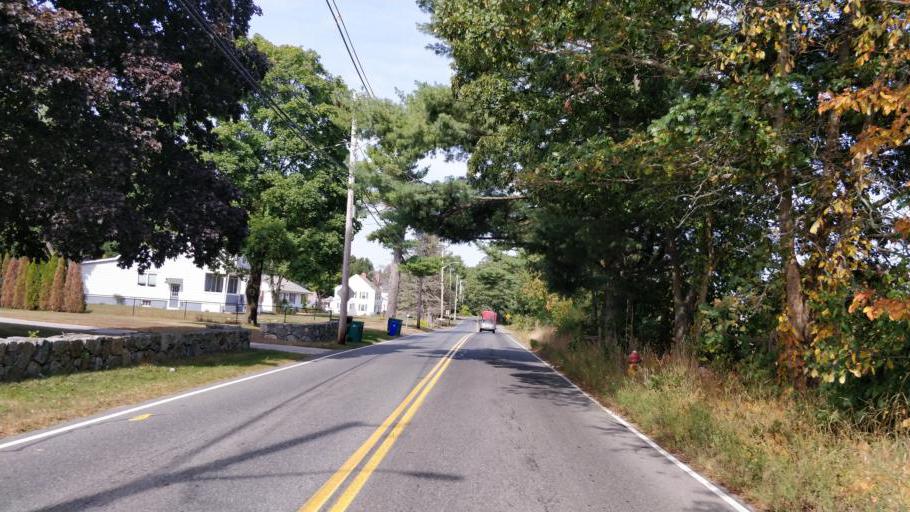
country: US
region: Massachusetts
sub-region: Bristol County
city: North Seekonk
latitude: 41.9036
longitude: -71.3337
